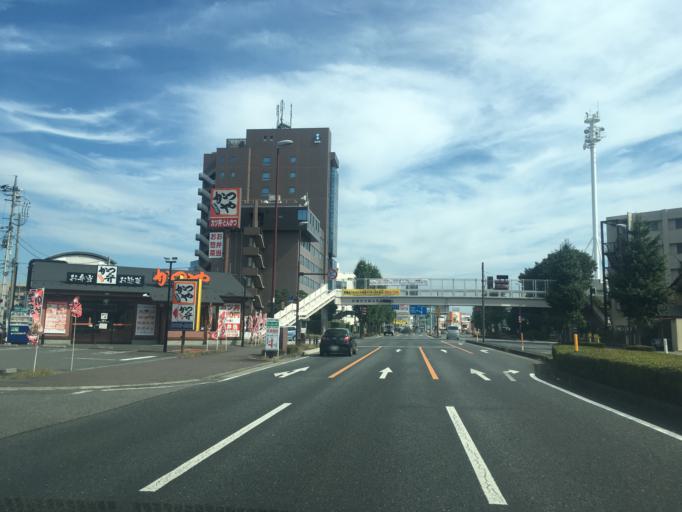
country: JP
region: Gunma
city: Maebashi-shi
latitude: 36.3842
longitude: 139.0439
